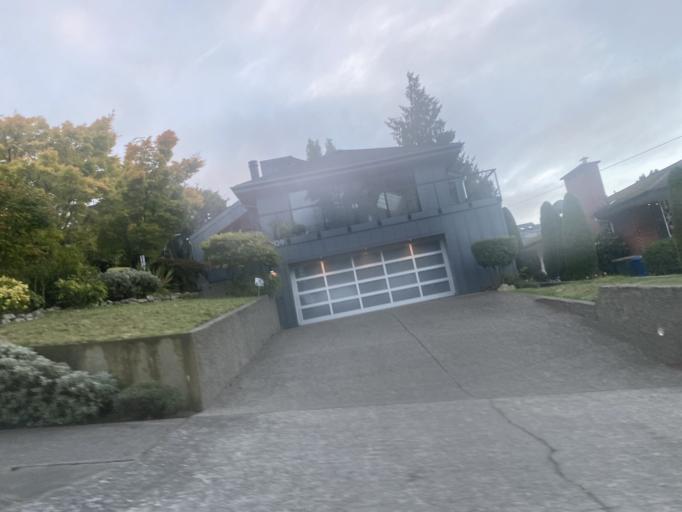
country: US
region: Washington
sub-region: King County
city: Seattle
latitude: 47.6505
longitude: -122.4071
